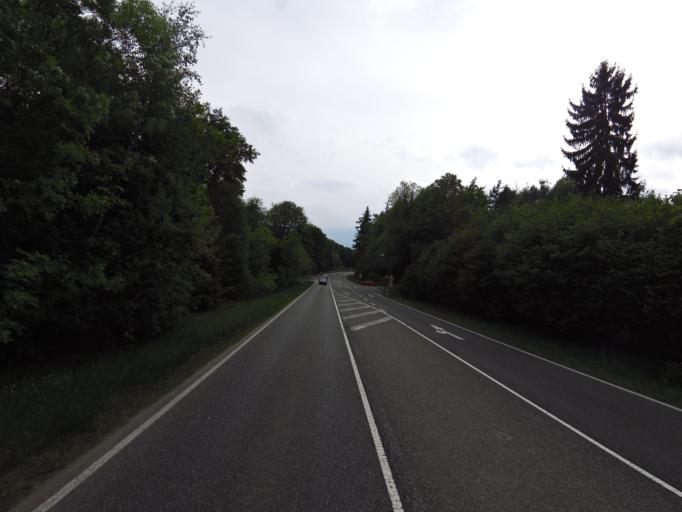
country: DE
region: Rheinland-Pfalz
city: Waldesch
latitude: 50.2585
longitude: 7.5270
